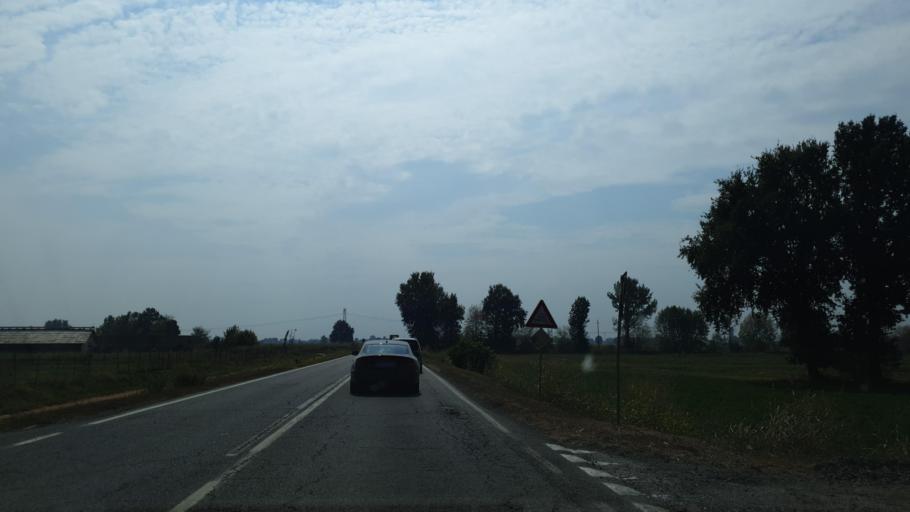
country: IT
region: Lombardy
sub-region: Provincia di Cremona
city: Pieve San Giacomo
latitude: 45.1174
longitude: 10.1887
